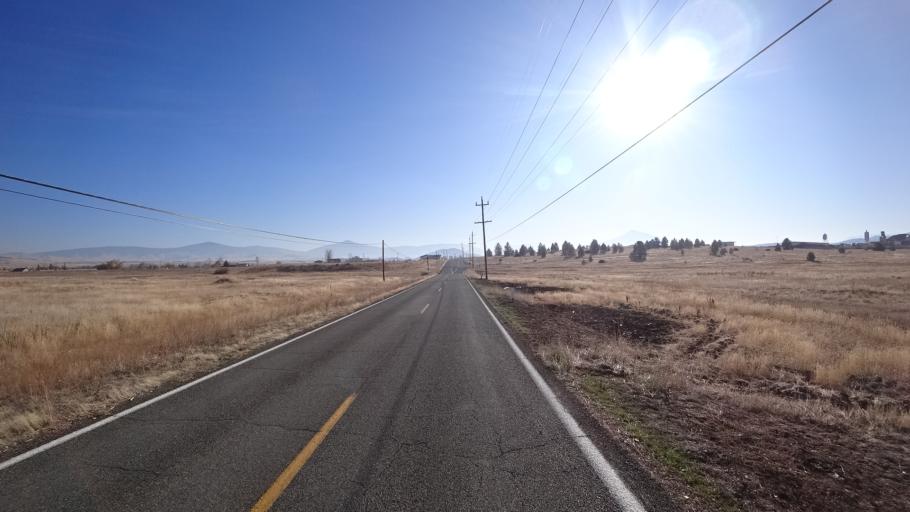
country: US
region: California
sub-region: Siskiyou County
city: Yreka
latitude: 41.7366
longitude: -122.5986
